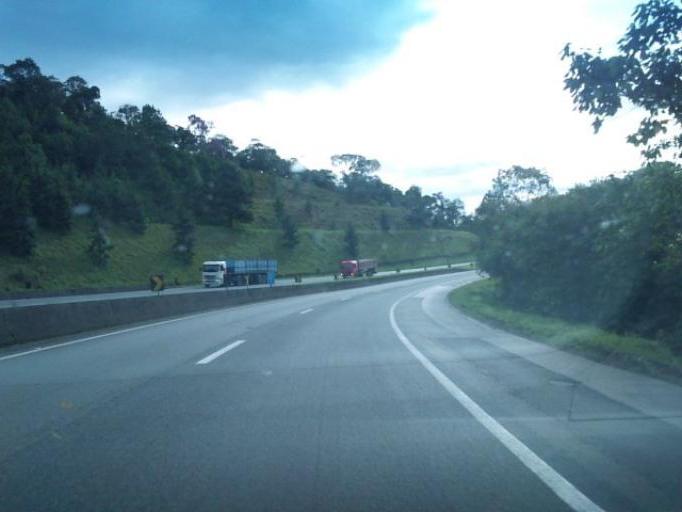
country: BR
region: Parana
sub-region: Antonina
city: Antonina
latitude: -25.1031
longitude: -48.7010
